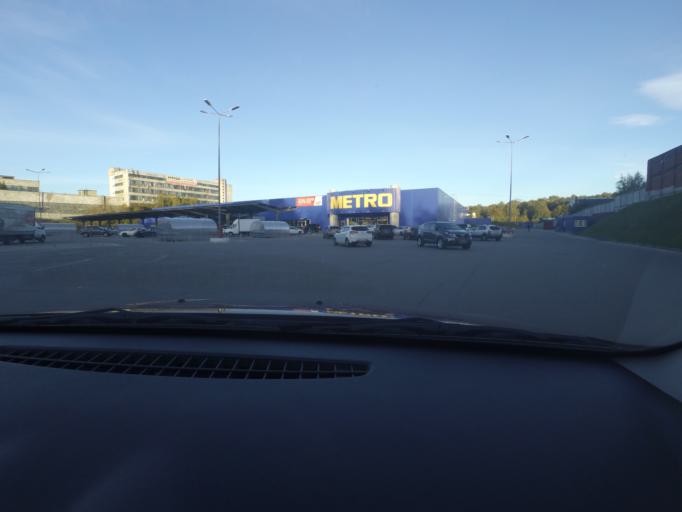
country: RU
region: Nizjnij Novgorod
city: Nizhniy Novgorod
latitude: 56.2864
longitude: 43.9958
